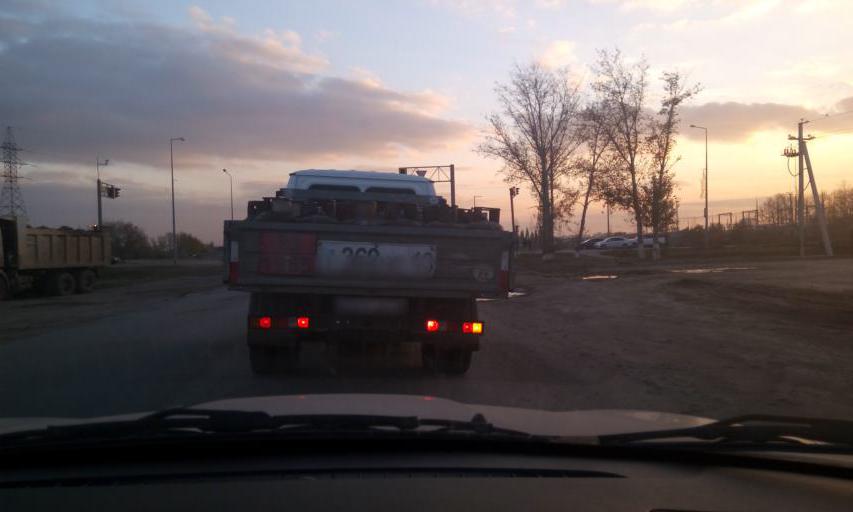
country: KZ
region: Astana Qalasy
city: Astana
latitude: 51.1389
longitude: 71.5291
